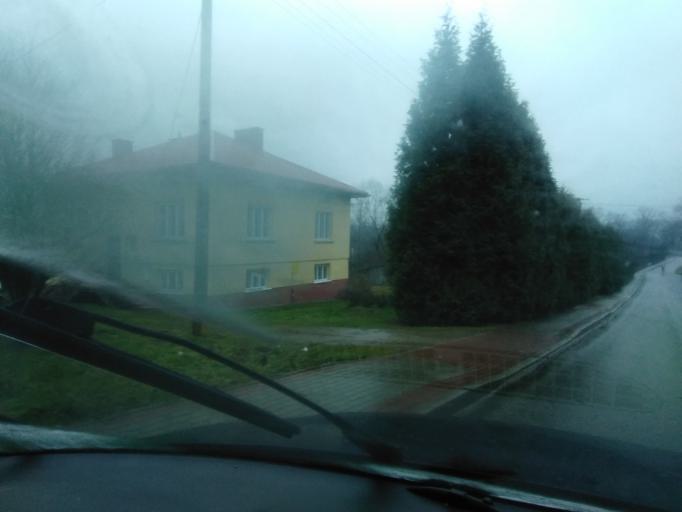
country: PL
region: Subcarpathian Voivodeship
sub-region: Powiat krosnienski
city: Kroscienko Wyzne
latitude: 49.6789
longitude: 21.8339
